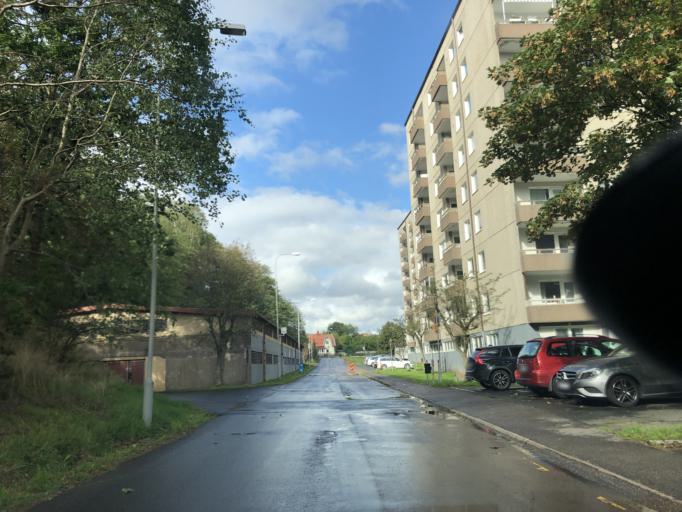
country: SE
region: Vaestra Goetaland
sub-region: Goteborg
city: Goeteborg
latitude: 57.7330
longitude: 11.9700
